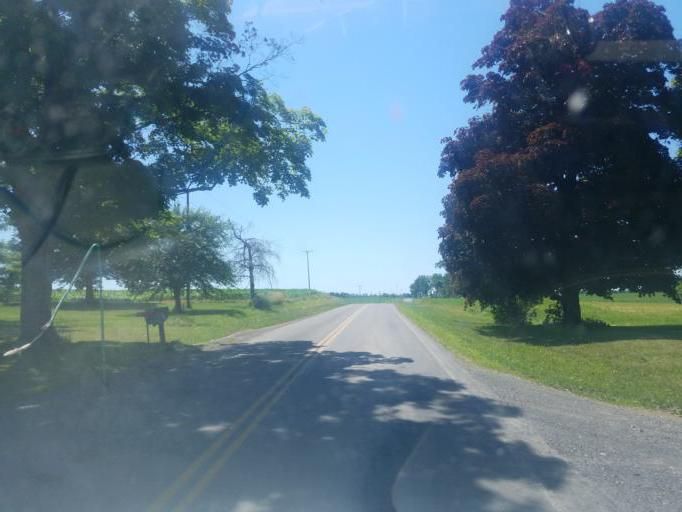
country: US
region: New York
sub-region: Ontario County
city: Geneva
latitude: 42.7989
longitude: -77.0248
